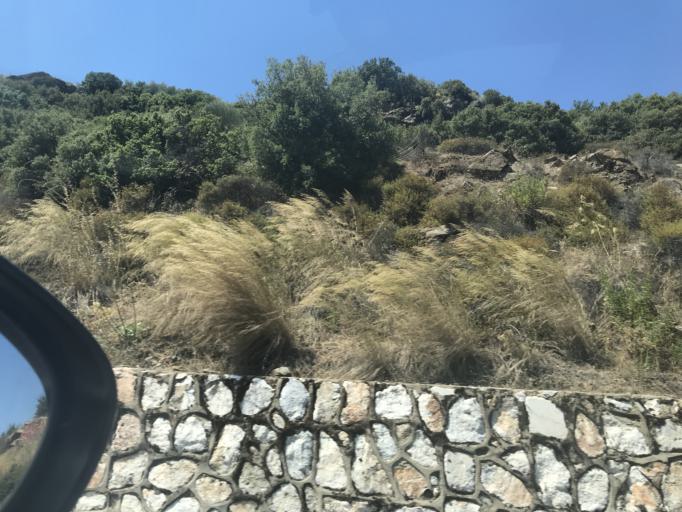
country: TR
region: Aydin
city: Akcaova
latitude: 37.5080
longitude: 28.1016
